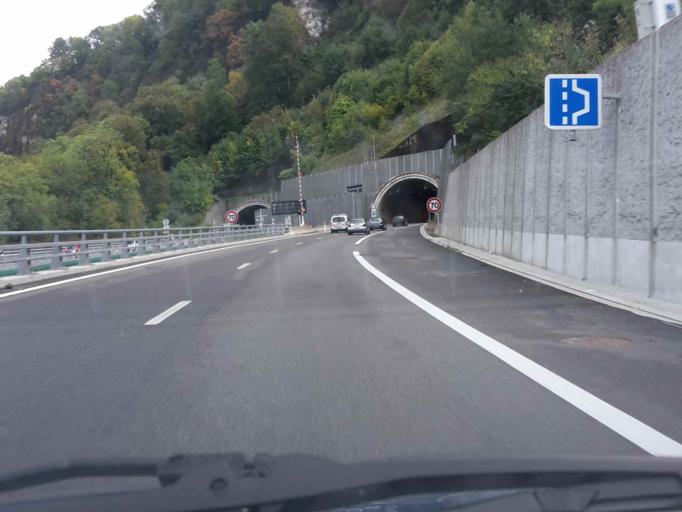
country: FR
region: Franche-Comte
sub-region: Departement du Doubs
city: Beure
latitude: 47.2159
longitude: 6.0196
